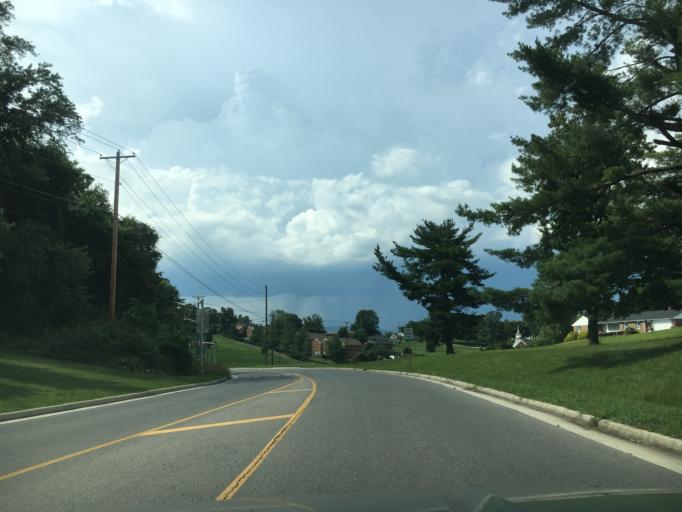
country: US
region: Virginia
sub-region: Roanoke County
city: Cave Spring
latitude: 37.2167
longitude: -80.0165
